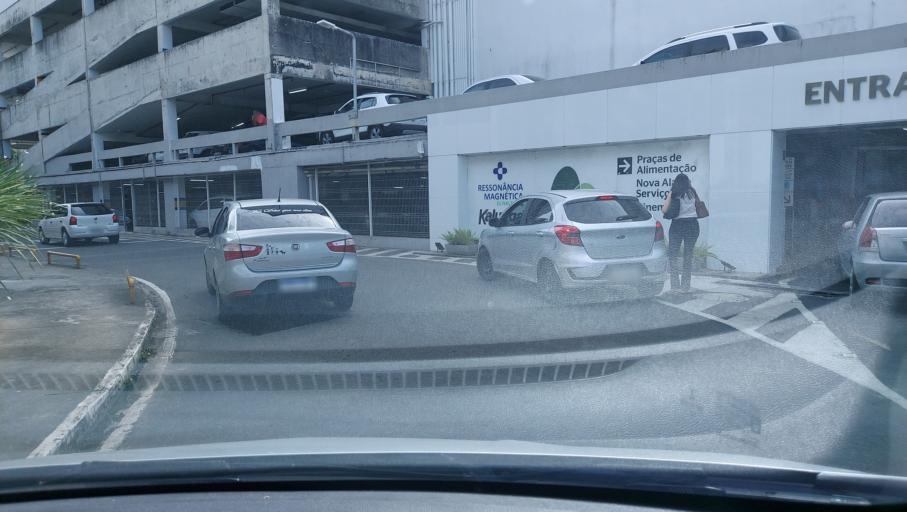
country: BR
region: Bahia
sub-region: Salvador
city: Salvador
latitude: -12.9824
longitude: -38.4629
